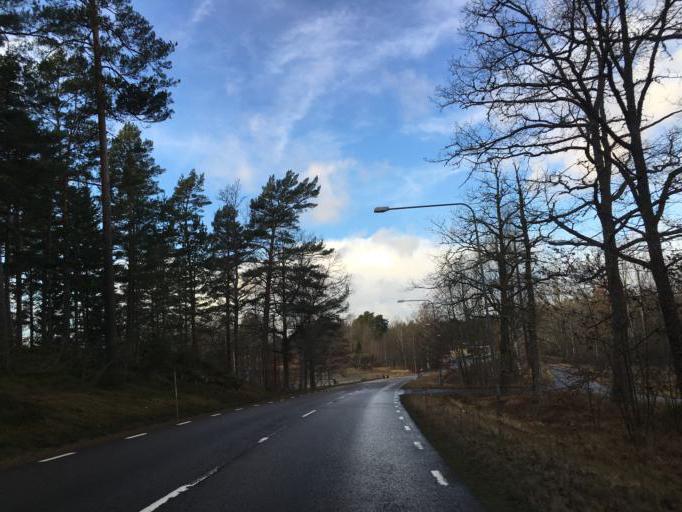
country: SE
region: Kalmar
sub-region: Vasterviks Kommun
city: Vaestervik
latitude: 57.7240
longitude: 16.5193
